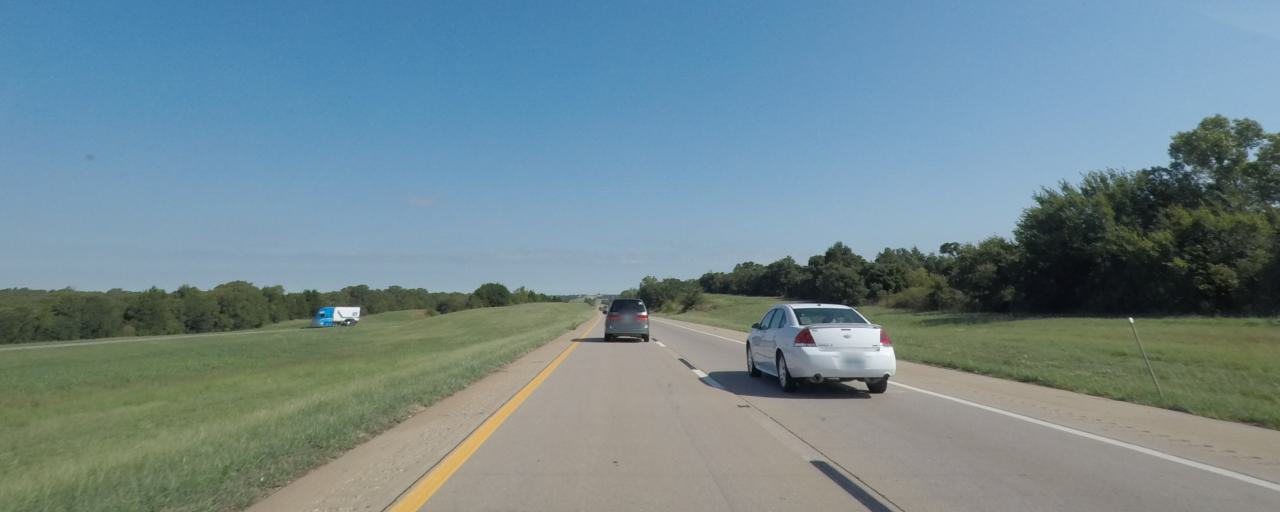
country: US
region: Oklahoma
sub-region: Logan County
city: Guthrie
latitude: 35.7695
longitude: -97.4159
